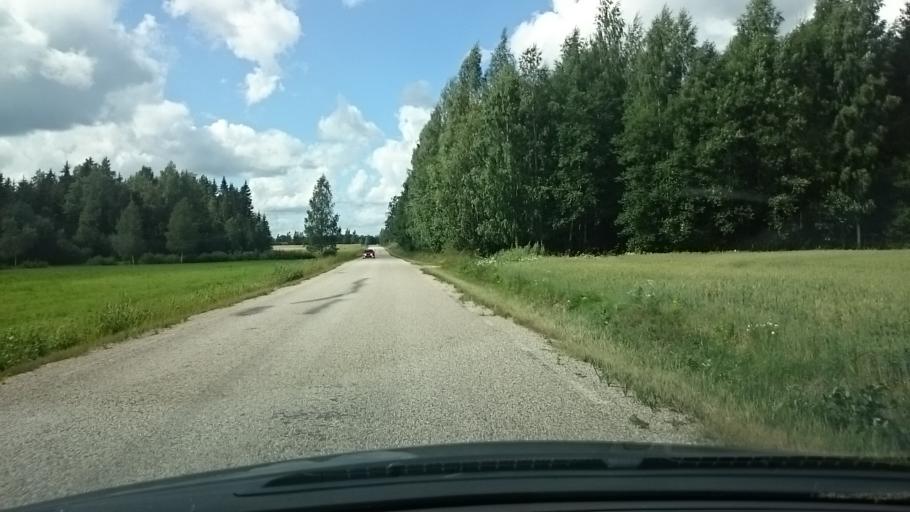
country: EE
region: Vorumaa
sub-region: Voru linn
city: Voru
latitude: 57.9193
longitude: 27.1512
